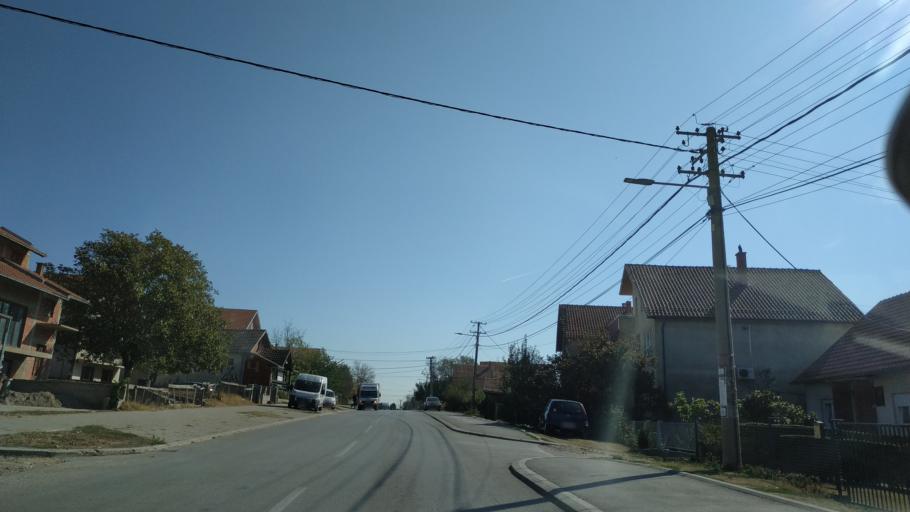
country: RS
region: Central Serbia
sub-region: Nisavski Okrug
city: Aleksinac
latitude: 43.5456
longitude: 21.6958
